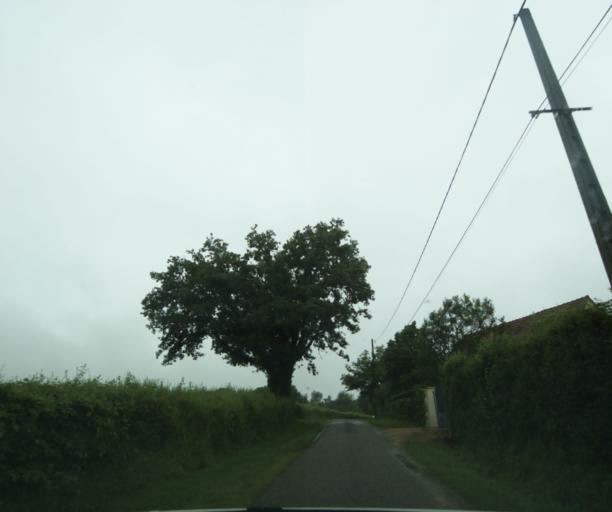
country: FR
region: Bourgogne
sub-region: Departement de Saone-et-Loire
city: Paray-le-Monial
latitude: 46.4066
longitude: 4.1849
